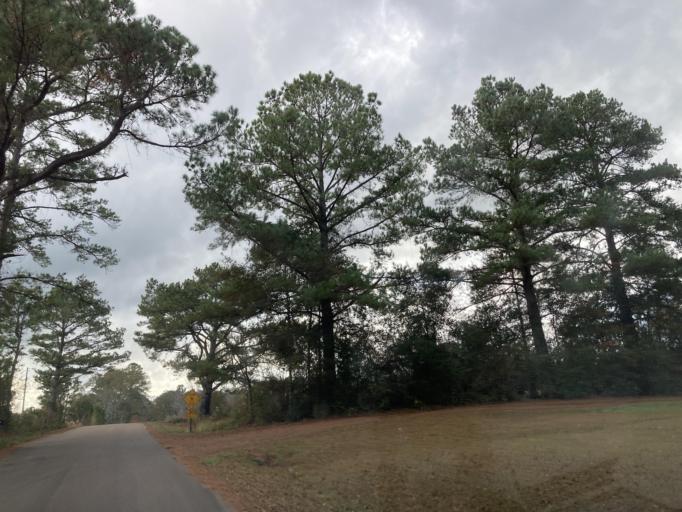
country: US
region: Mississippi
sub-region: Lamar County
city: Purvis
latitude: 31.1639
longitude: -89.6158
